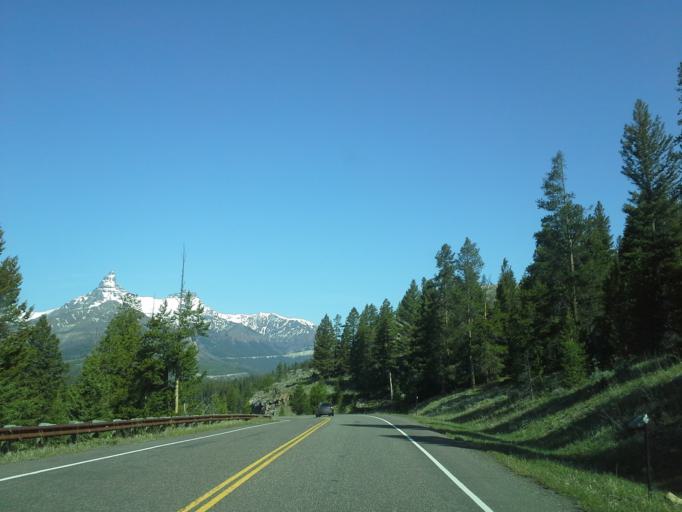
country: US
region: Montana
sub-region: Carbon County
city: Red Lodge
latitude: 44.9451
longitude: -109.7809
